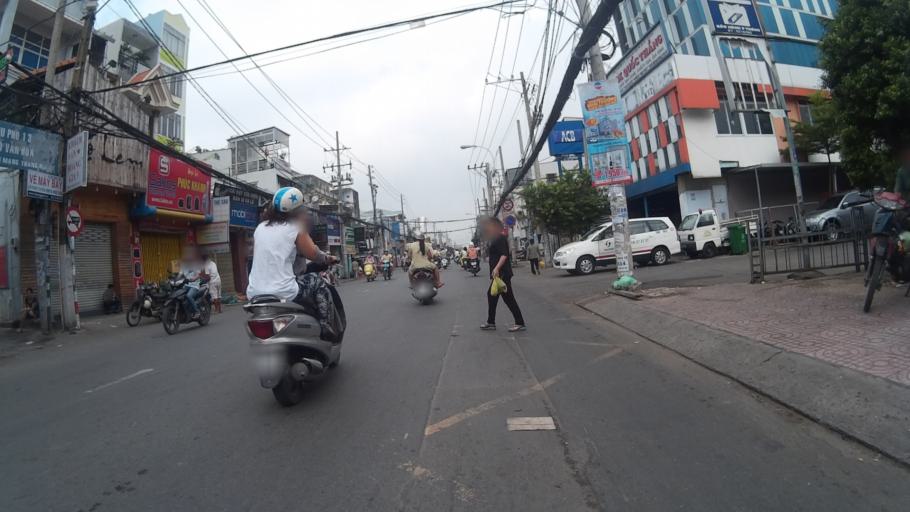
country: VN
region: Ho Chi Minh City
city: Quan Phu Nhuan
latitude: 10.7841
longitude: 106.6701
